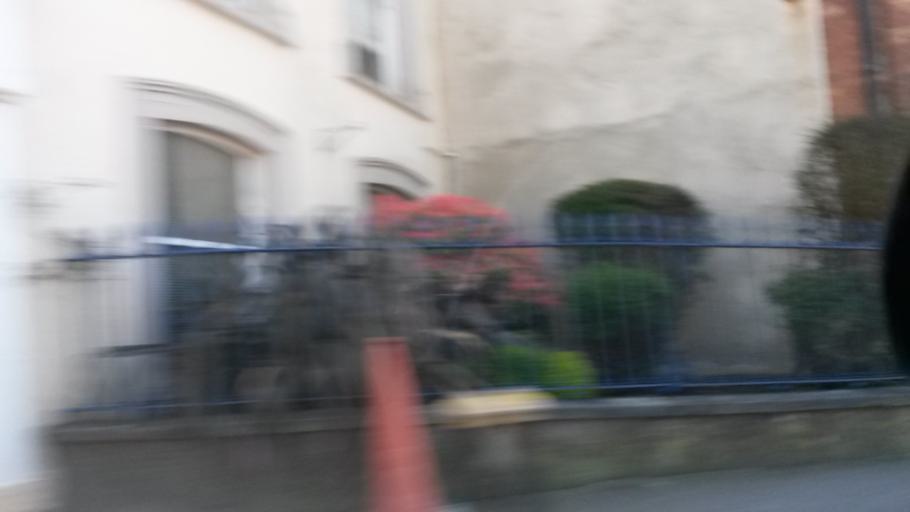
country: IE
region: Munster
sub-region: County Cork
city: Cork
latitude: 51.8998
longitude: -8.4832
